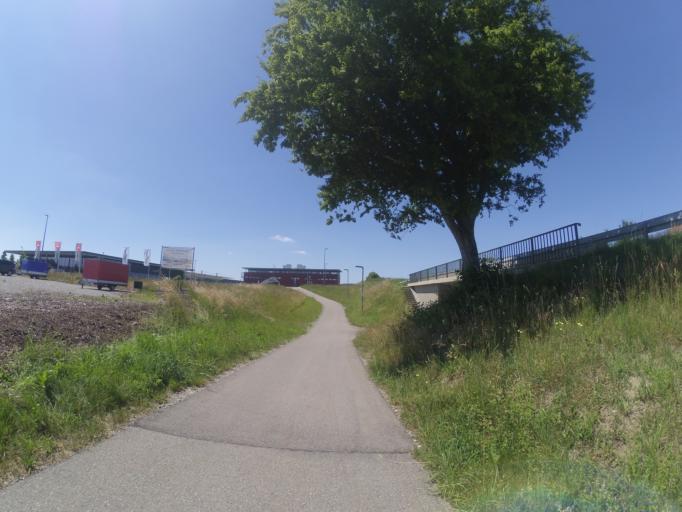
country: DE
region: Baden-Wuerttemberg
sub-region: Tuebingen Region
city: Aulendorf
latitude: 47.9386
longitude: 9.6548
